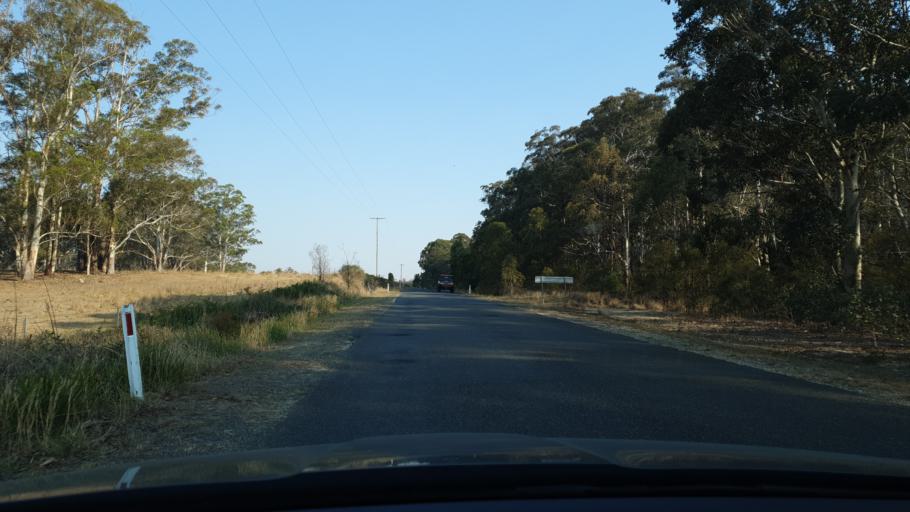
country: AU
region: New South Wales
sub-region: Tenterfield Municipality
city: Carrolls Creek
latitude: -28.6909
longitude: 152.0881
